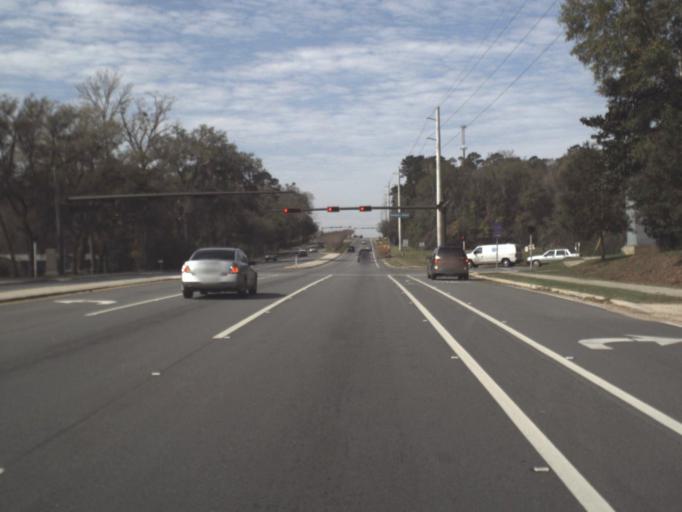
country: US
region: Florida
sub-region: Leon County
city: Tallahassee
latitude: 30.4669
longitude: -84.2093
